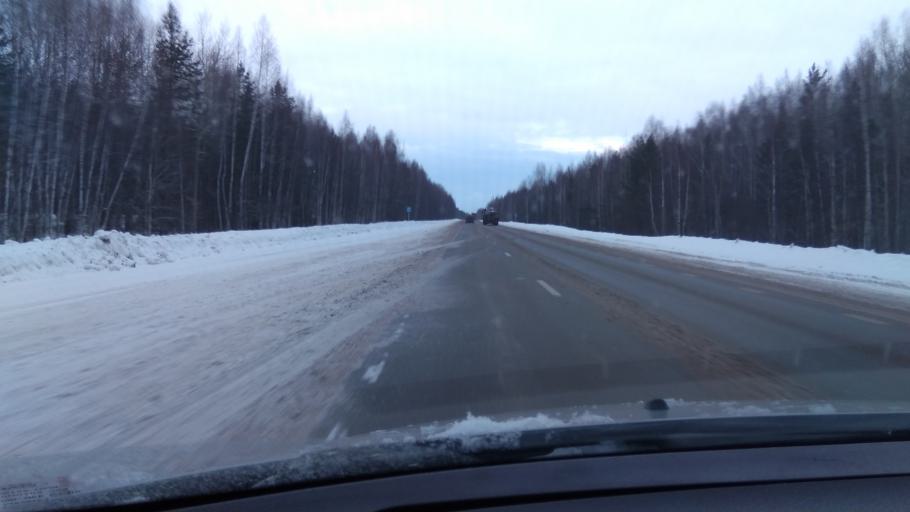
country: RU
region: Sverdlovsk
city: Tsementnyy
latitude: 57.4170
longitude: 60.2109
